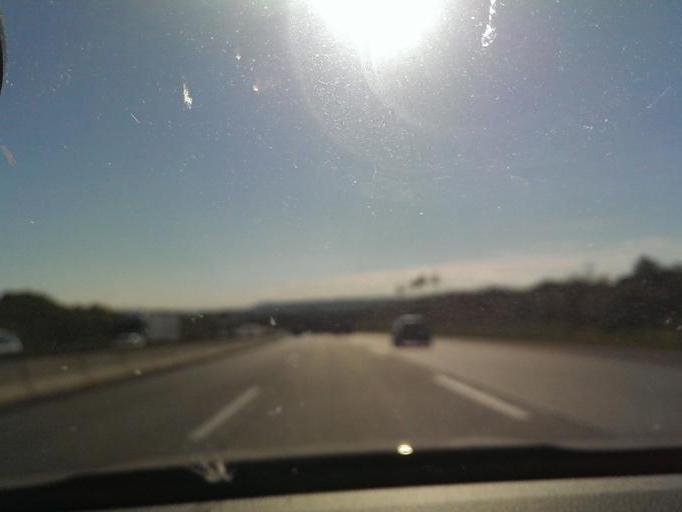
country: DE
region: Baden-Wuerttemberg
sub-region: Regierungsbezirk Stuttgart
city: Rutesheim
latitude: 48.8031
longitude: 8.9357
